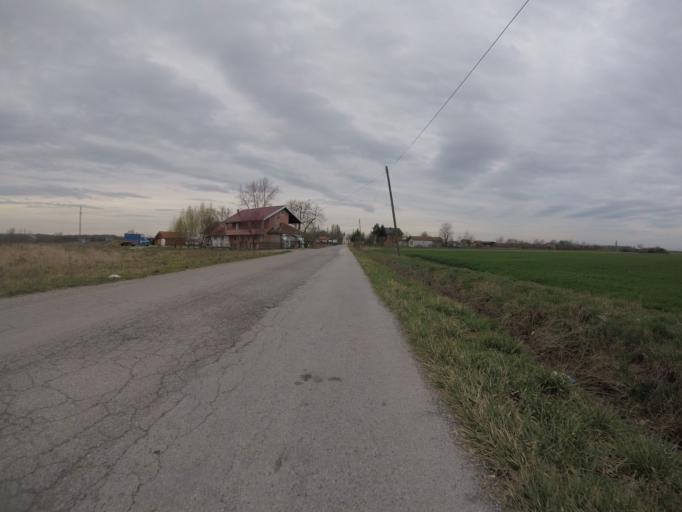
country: HR
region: Zagrebacka
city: Lukavec
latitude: 45.7047
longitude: 16.0072
